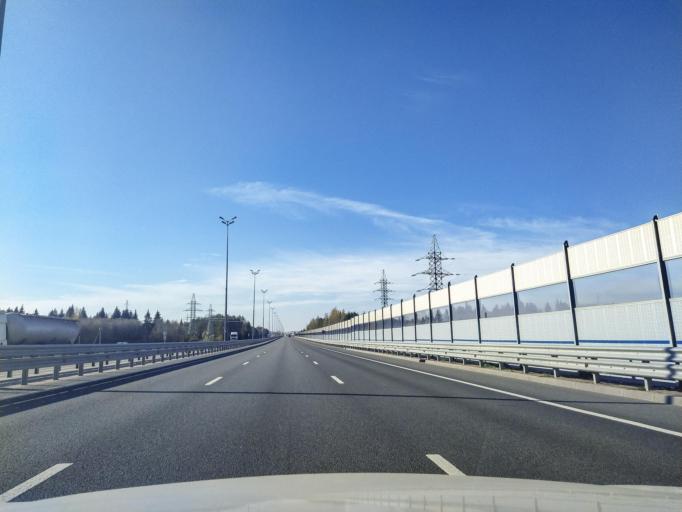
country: RU
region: Leningrad
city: Gatchina
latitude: 59.5269
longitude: 30.1164
